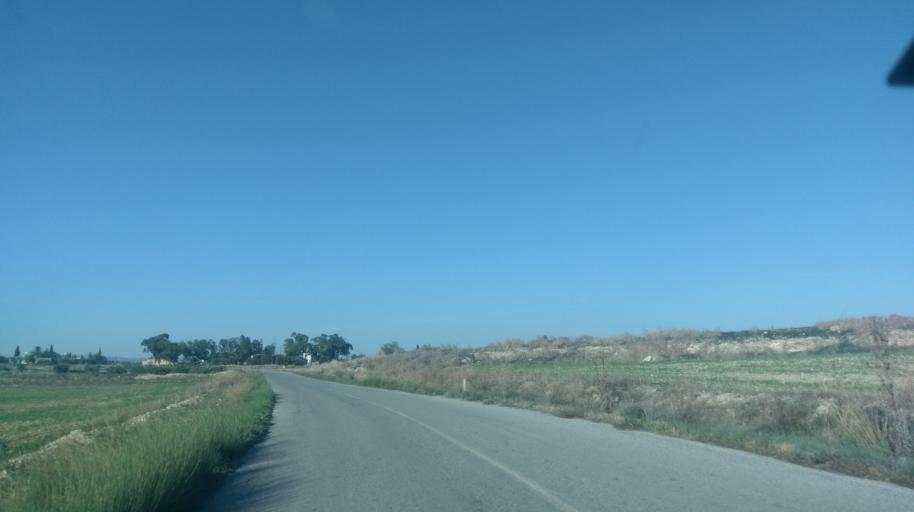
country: CY
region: Ammochostos
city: Lefkonoiko
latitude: 35.2119
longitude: 33.6986
